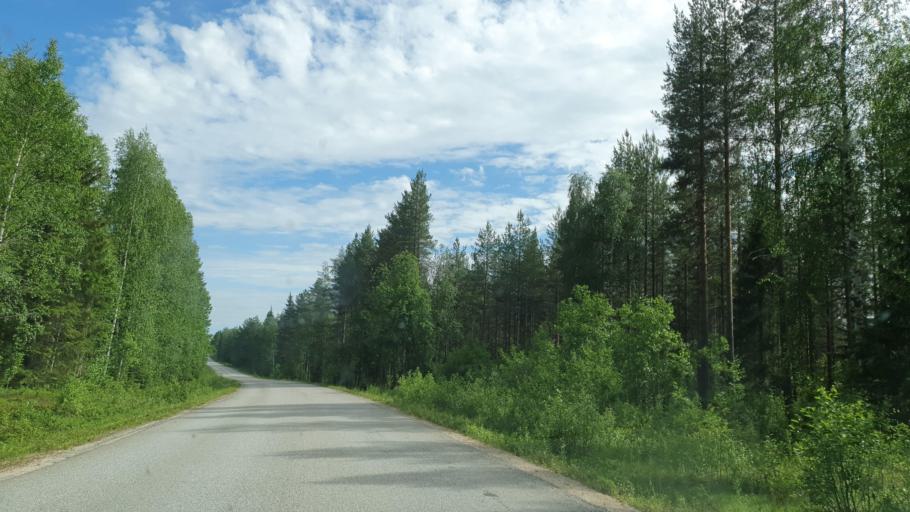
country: FI
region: Kainuu
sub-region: Kehys-Kainuu
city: Suomussalmi
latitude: 64.5928
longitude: 29.1012
